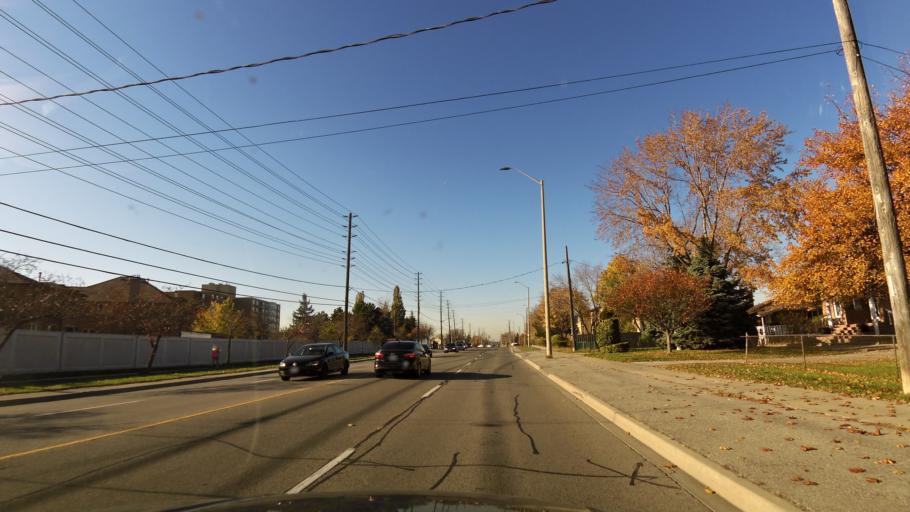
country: CA
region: Ontario
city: Mississauga
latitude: 43.6151
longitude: -79.6137
